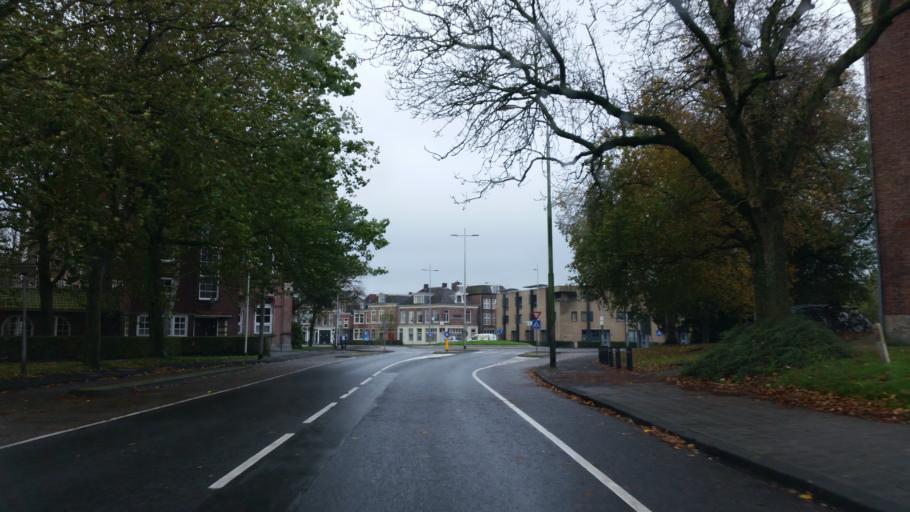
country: NL
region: Friesland
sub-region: Gemeente Leeuwarden
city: Bilgaard
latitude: 53.2061
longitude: 5.7973
